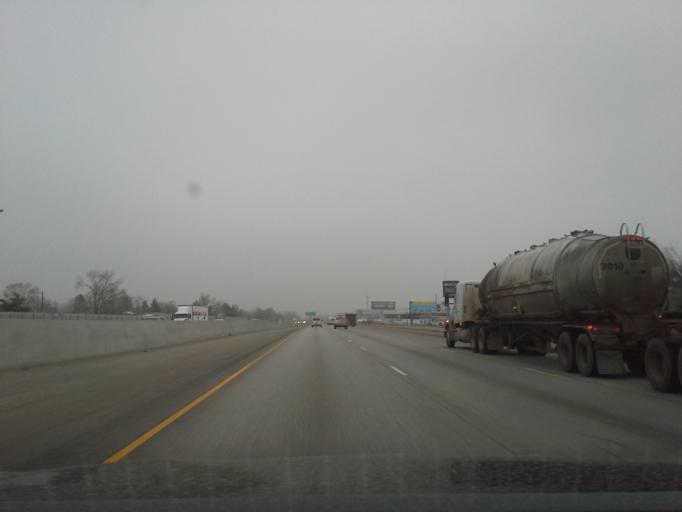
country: US
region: Utah
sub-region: Davis County
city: Layton
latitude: 41.0708
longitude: -111.9740
